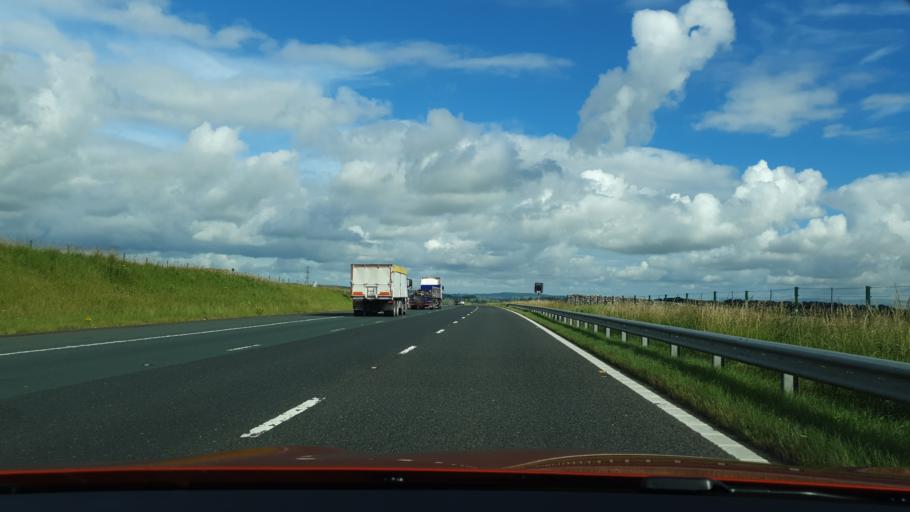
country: GB
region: England
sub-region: Cumbria
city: Penrith
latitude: 54.5380
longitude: -2.6620
